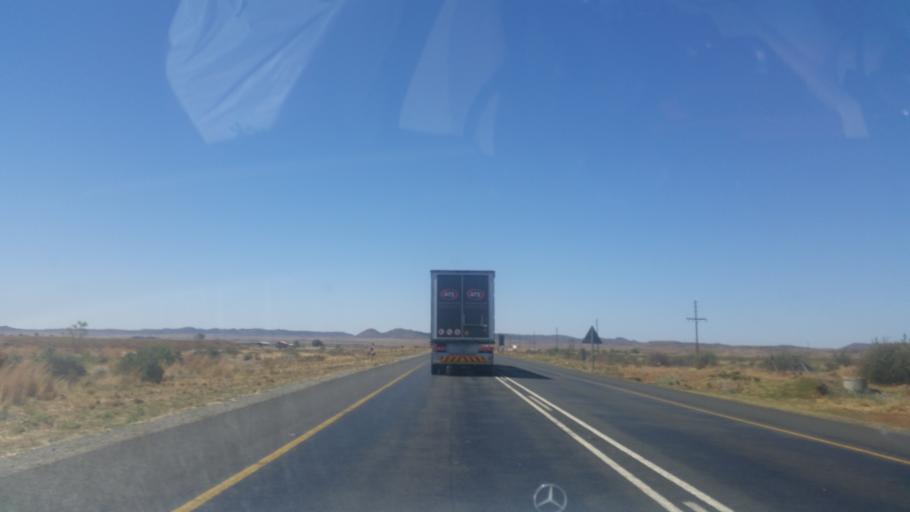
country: ZA
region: Northern Cape
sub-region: Pixley ka Seme District Municipality
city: Colesberg
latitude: -30.7051
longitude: 25.1152
